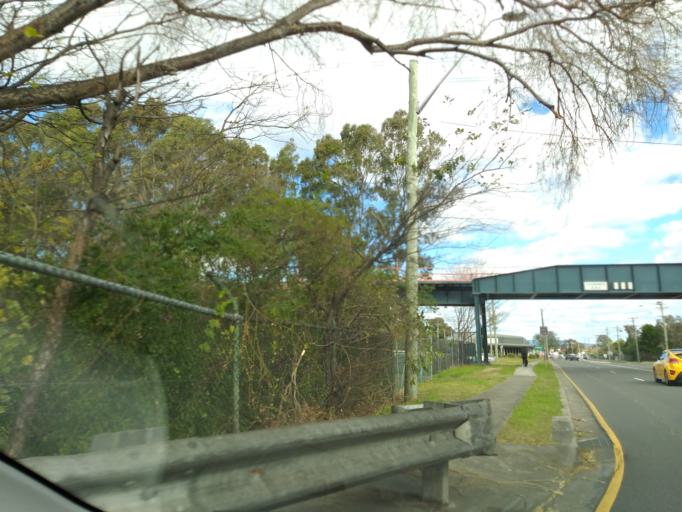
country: AU
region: New South Wales
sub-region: Wollongong
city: Cordeaux Heights
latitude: -34.4475
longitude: 150.8516
